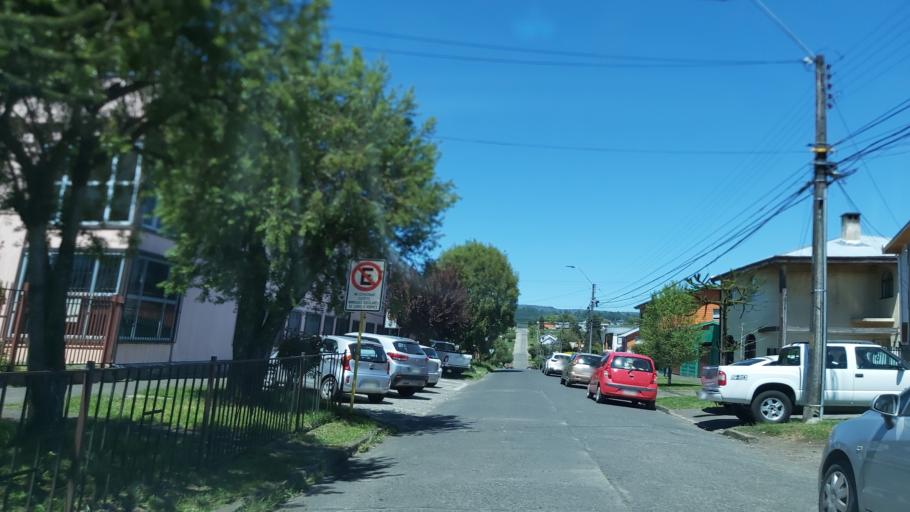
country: CL
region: Araucania
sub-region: Provincia de Cautin
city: Vilcun
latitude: -38.4382
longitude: -71.8891
